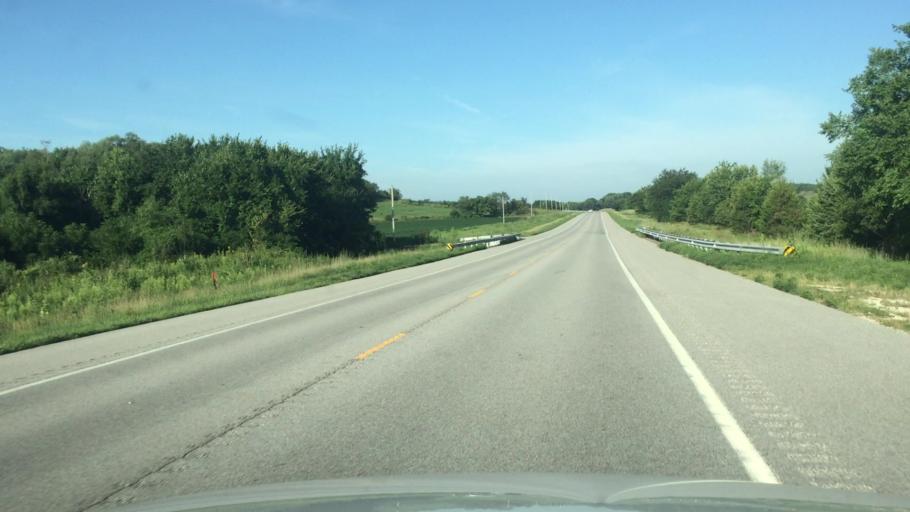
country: US
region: Kansas
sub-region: Miami County
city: Osawatomie
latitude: 38.3932
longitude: -95.0936
